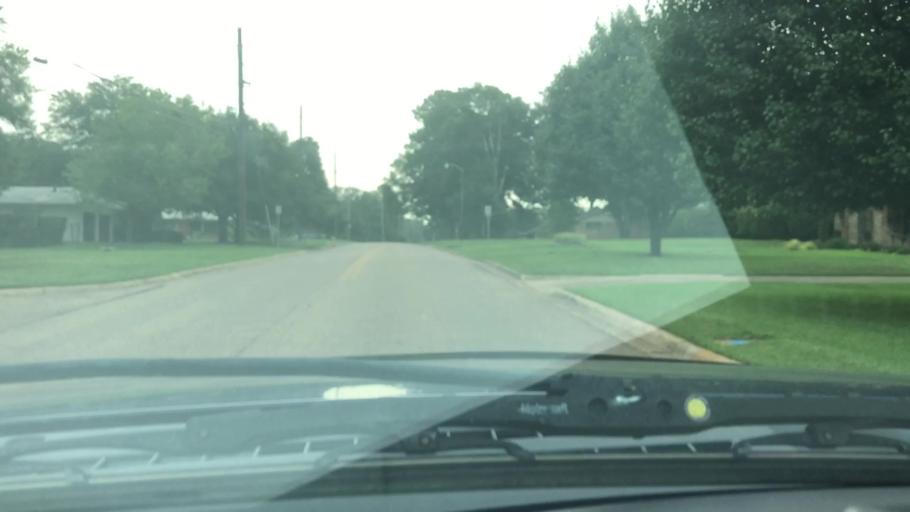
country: US
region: Arkansas
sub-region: Miller County
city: Texarkana
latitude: 33.4606
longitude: -94.0646
